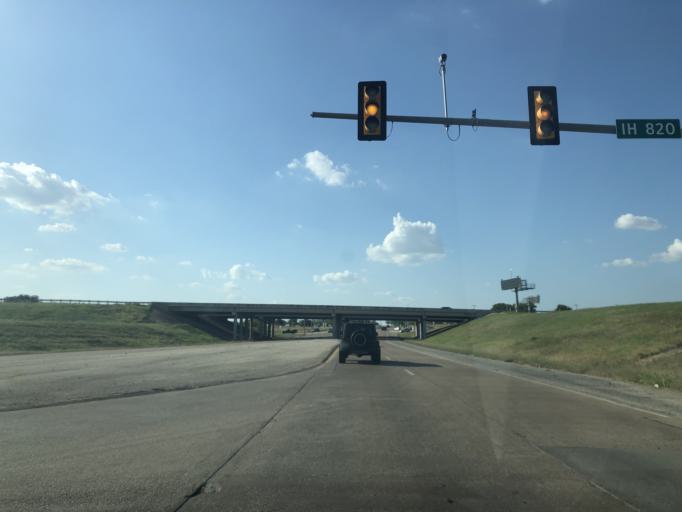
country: US
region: Texas
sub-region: Tarrant County
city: Sansom Park
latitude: 32.8252
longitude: -97.3846
